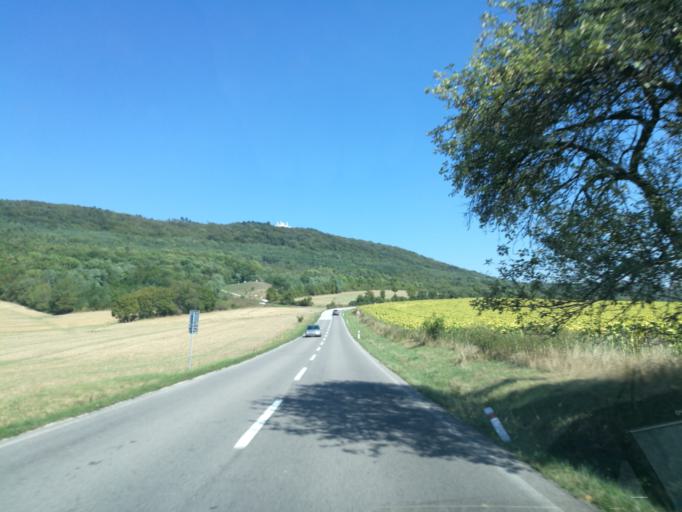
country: SK
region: Nitriansky
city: Brezova pod Bradlom
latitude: 48.6693
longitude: 17.5534
